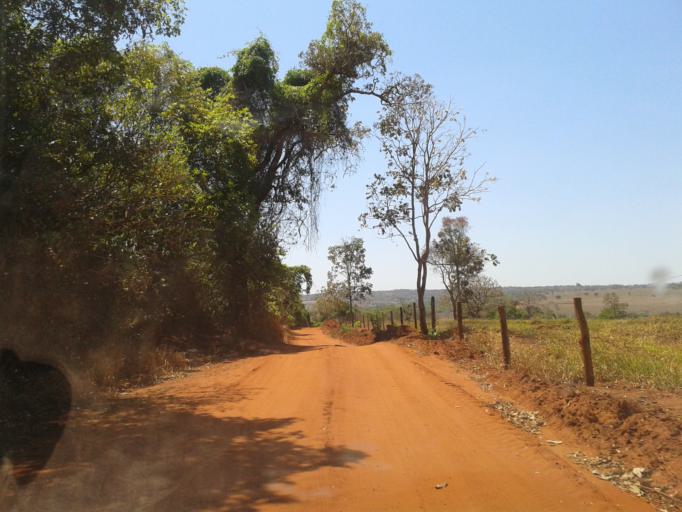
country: BR
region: Minas Gerais
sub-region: Ituiutaba
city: Ituiutaba
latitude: -19.0696
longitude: -49.3291
